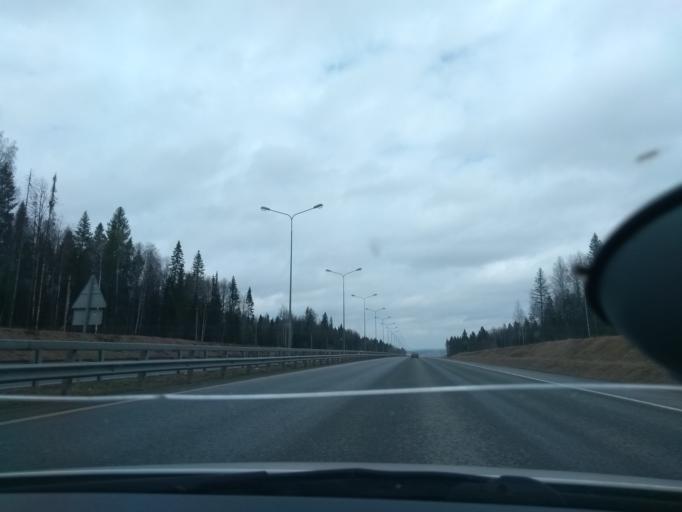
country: RU
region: Perm
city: Zvezdnyy
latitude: 57.7566
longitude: 56.3333
